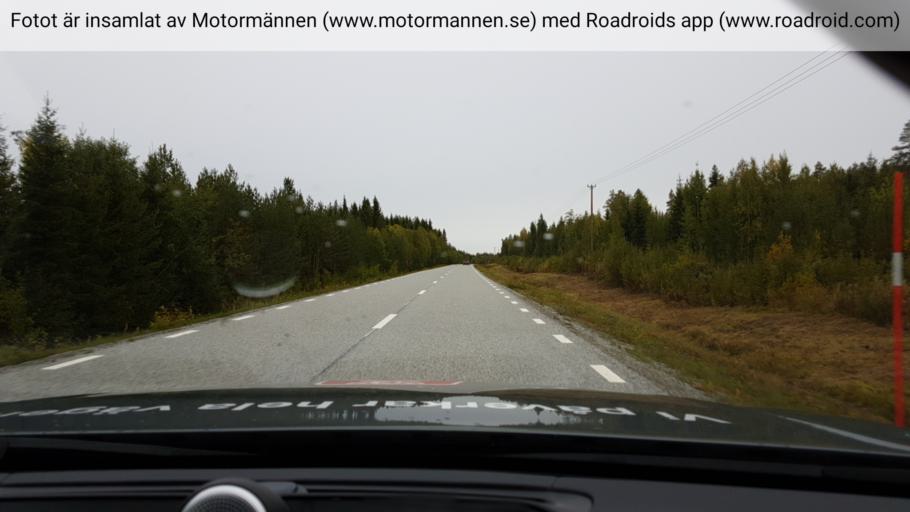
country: SE
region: Jaemtland
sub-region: Stroemsunds Kommun
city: Stroemsund
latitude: 63.9469
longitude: 15.4853
